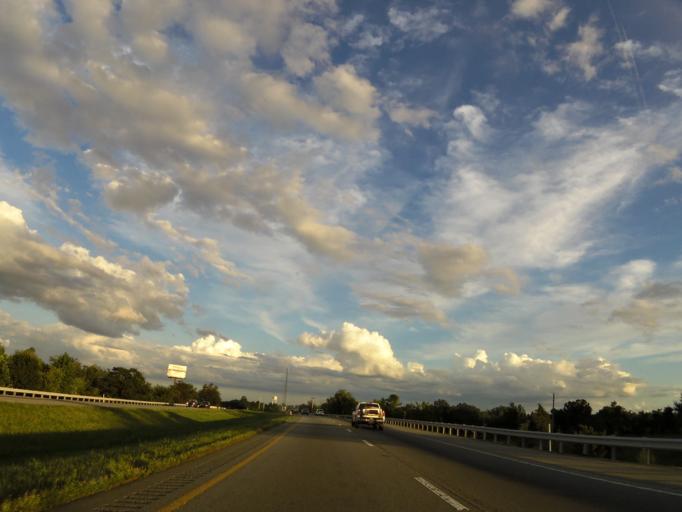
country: US
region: Tennessee
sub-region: Putnam County
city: Monterey
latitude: 36.1026
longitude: -85.2398
